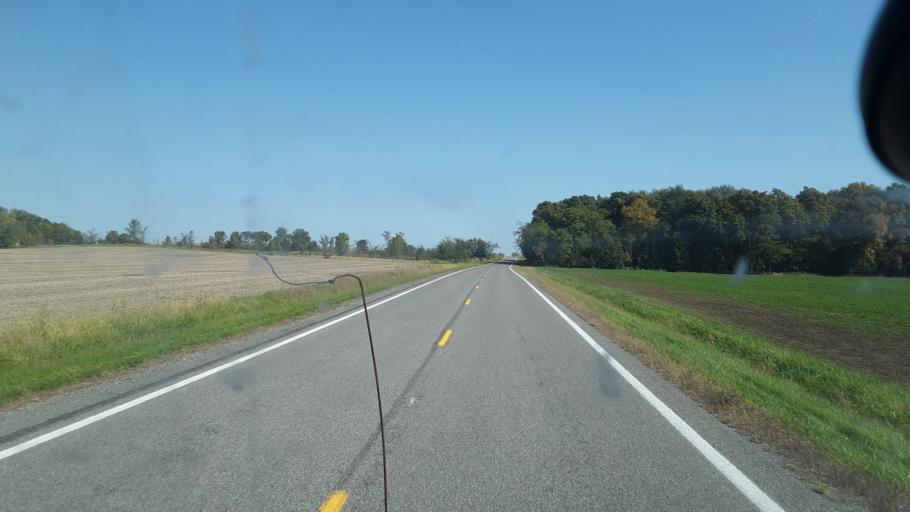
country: US
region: Ohio
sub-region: Logan County
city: Northwood
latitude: 40.5084
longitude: -83.6498
